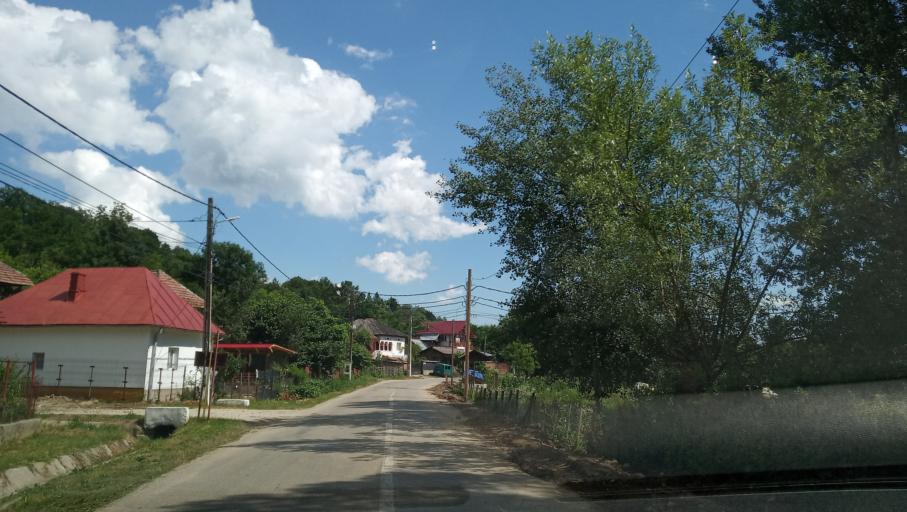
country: RO
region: Valcea
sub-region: Comuna Stoenesti
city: Stoenesti
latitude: 45.1392
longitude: 24.1462
